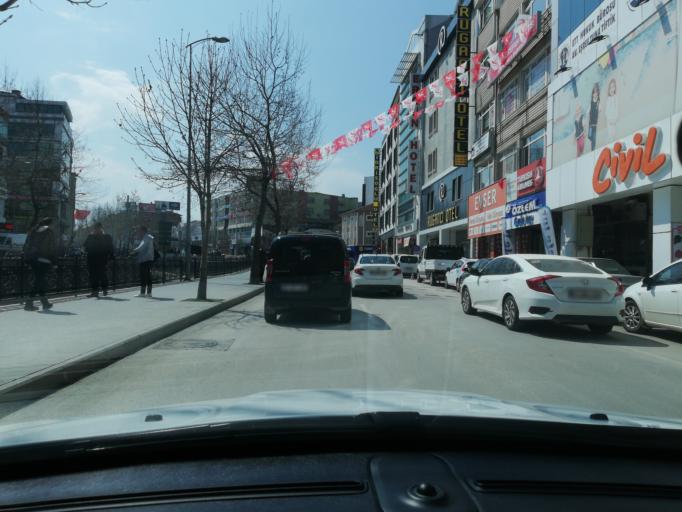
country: TR
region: Kastamonu
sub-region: Cide
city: Kastamonu
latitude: 41.3795
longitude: 33.7775
